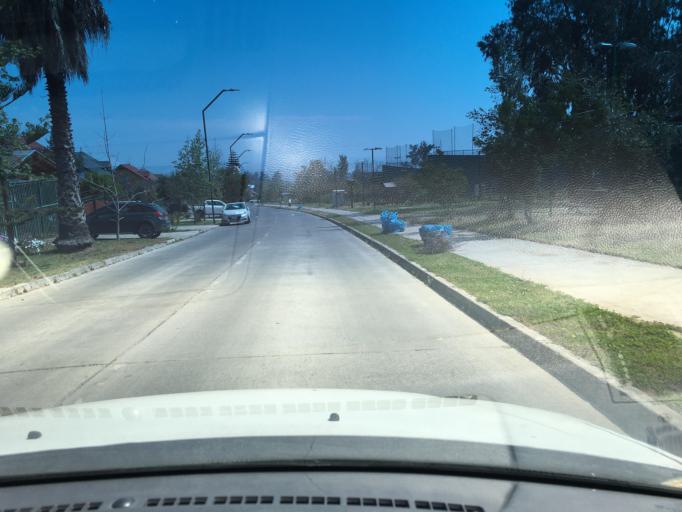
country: CL
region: Santiago Metropolitan
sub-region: Provincia de Santiago
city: Villa Presidente Frei, Nunoa, Santiago, Chile
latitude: -33.5106
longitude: -70.5307
